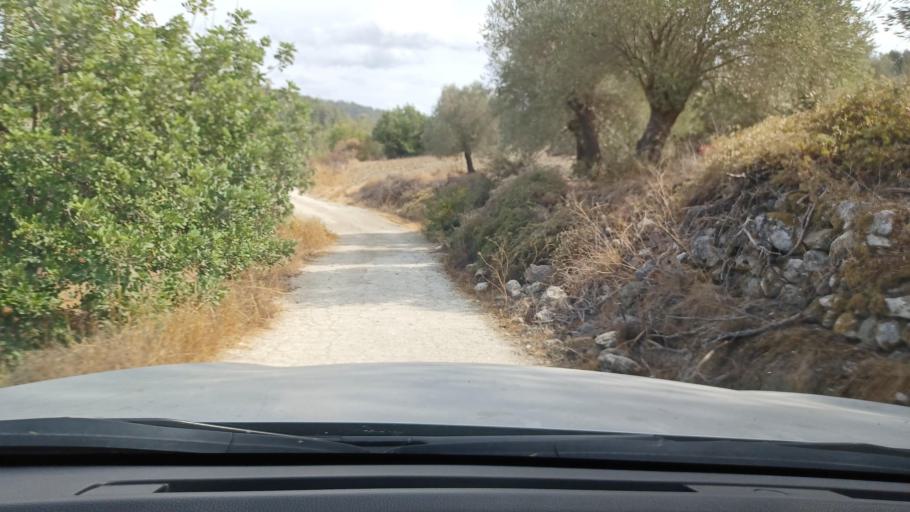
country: CY
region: Pafos
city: Polis
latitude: 35.0006
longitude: 32.5258
